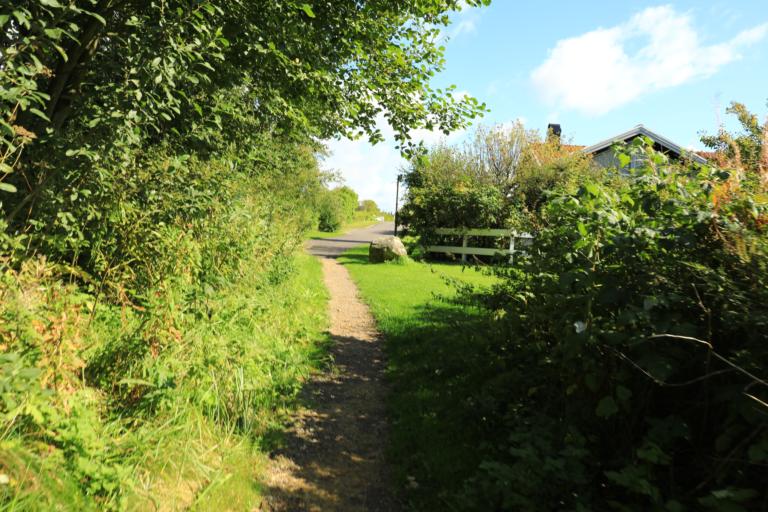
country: SE
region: Halland
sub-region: Varbergs Kommun
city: Traslovslage
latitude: 57.0789
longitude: 12.2682
